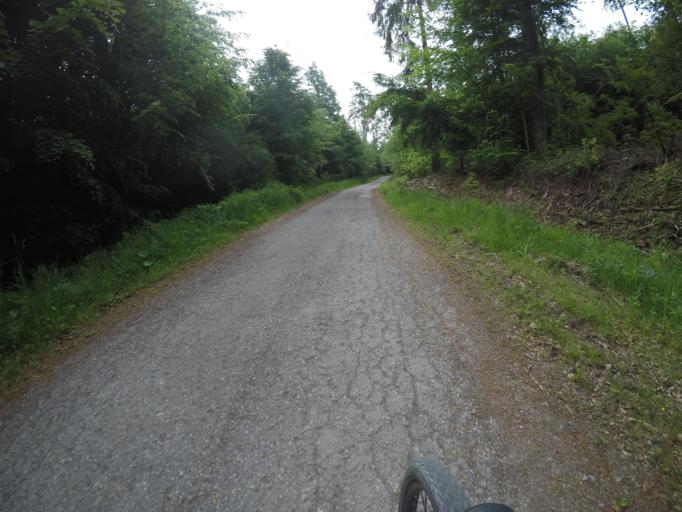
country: DE
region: Baden-Wuerttemberg
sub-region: Regierungsbezirk Stuttgart
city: Schlaitdorf
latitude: 48.6026
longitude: 9.1748
